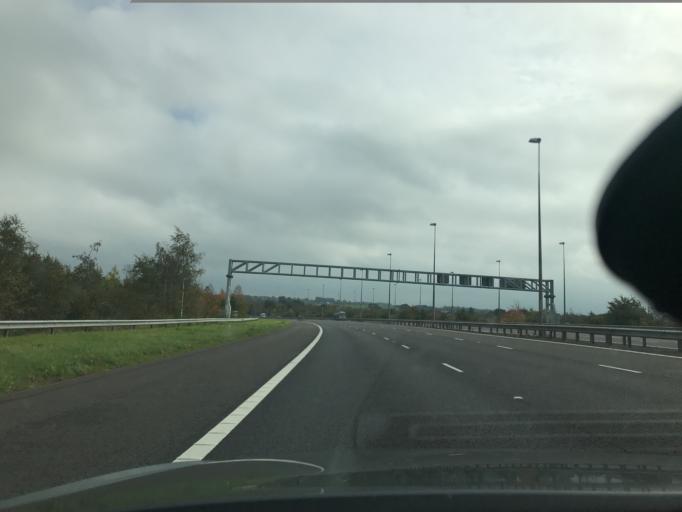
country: GB
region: England
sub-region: Staffordshire
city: Featherstone
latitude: 52.6662
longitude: -2.0676
